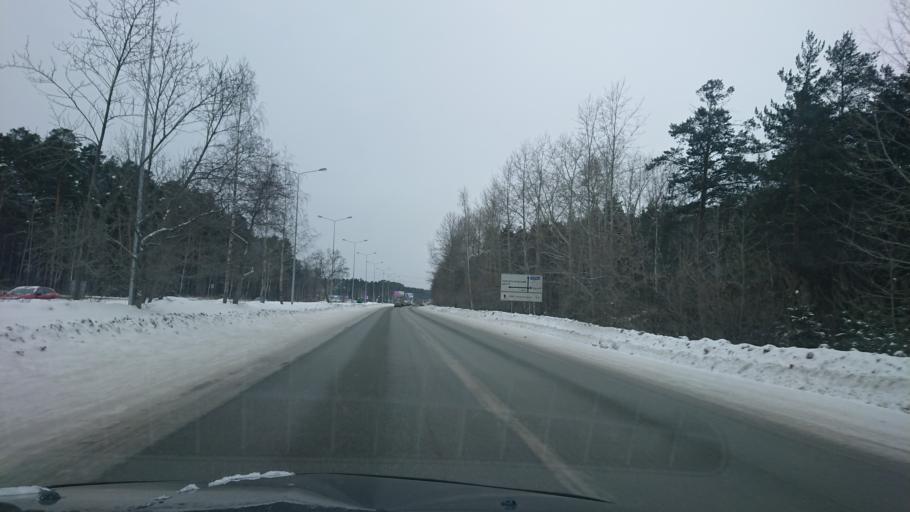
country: RU
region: Sverdlovsk
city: Shirokaya Rechka
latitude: 56.8101
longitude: 60.5243
